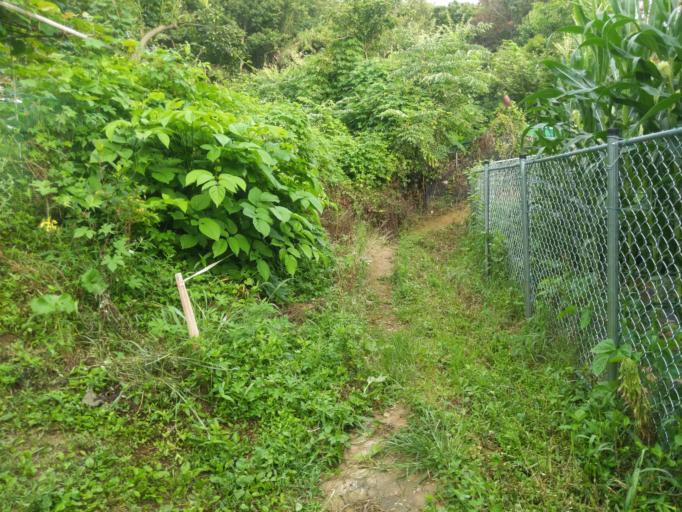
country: KR
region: Daegu
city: Hwawon
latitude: 35.8019
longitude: 128.5265
